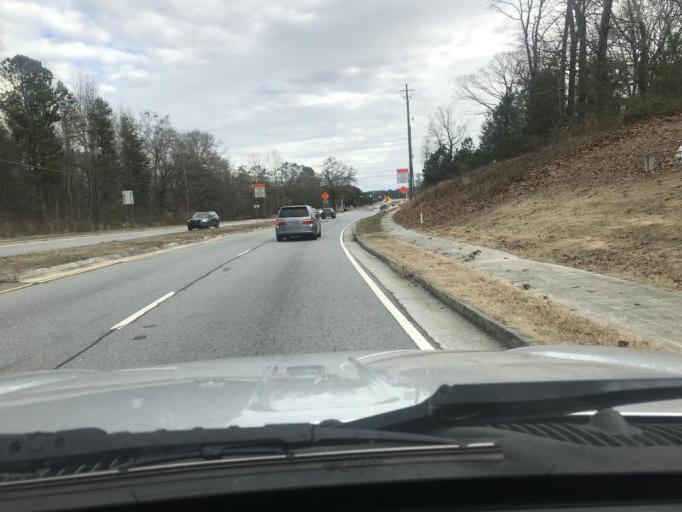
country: US
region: Georgia
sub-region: Gwinnett County
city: Buford
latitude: 34.0673
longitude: -83.9522
